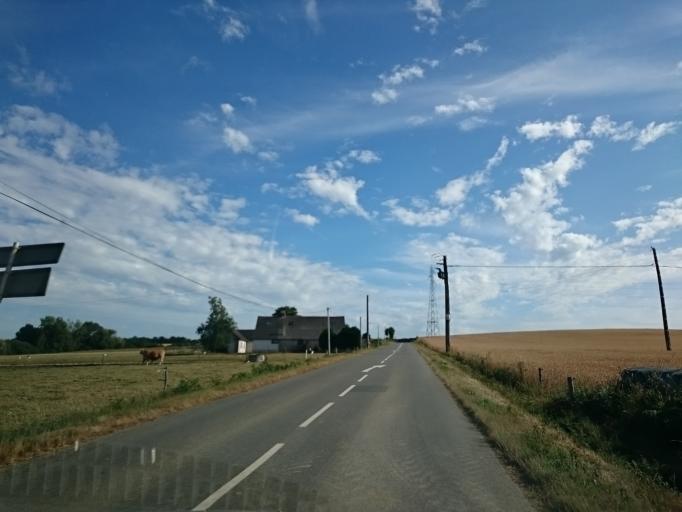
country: FR
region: Brittany
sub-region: Departement d'Ille-et-Vilaine
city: Chanteloup
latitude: 47.9257
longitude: -1.6172
